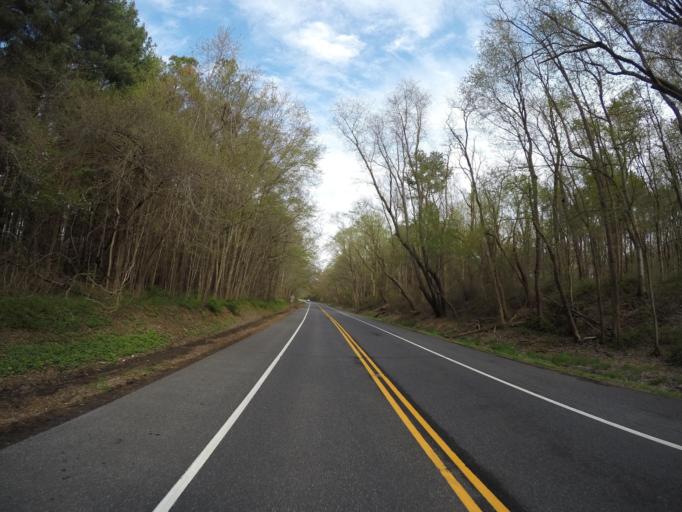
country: US
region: Delaware
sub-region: New Castle County
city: Glasgow
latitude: 39.5470
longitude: -75.7249
